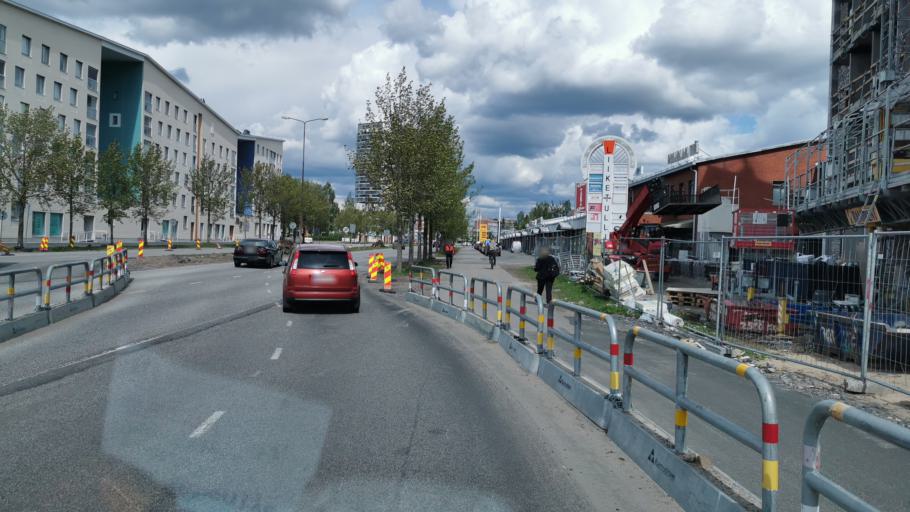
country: FI
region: Northern Ostrobothnia
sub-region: Oulu
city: Oulu
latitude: 65.0009
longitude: 25.4641
